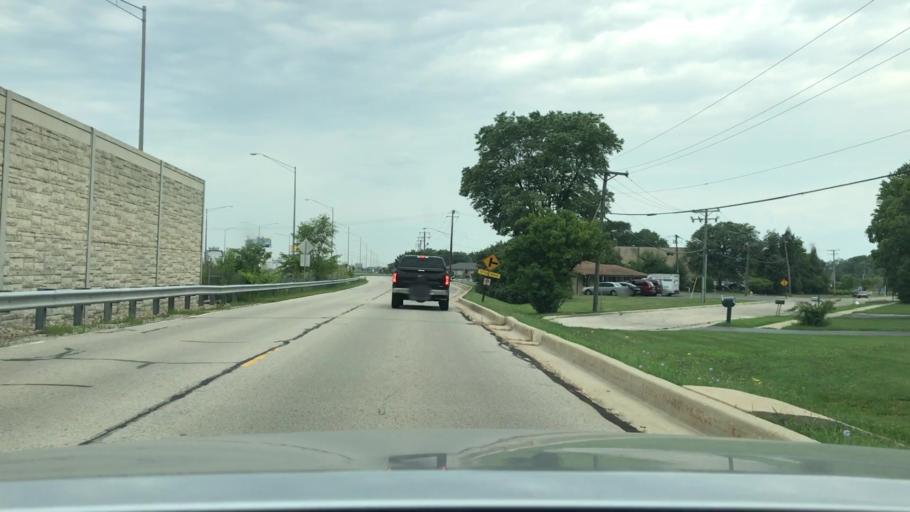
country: US
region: Illinois
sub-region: Will County
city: Bolingbrook
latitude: 41.6992
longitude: -88.0416
